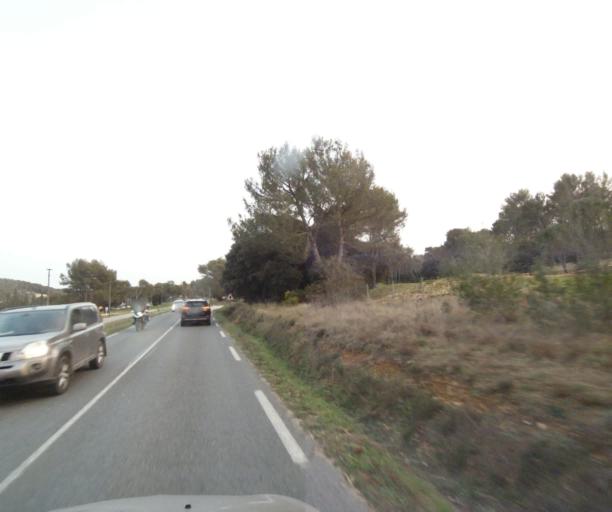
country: FR
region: Provence-Alpes-Cote d'Azur
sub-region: Departement des Bouches-du-Rhone
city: Cabries
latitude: 43.4537
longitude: 5.3573
